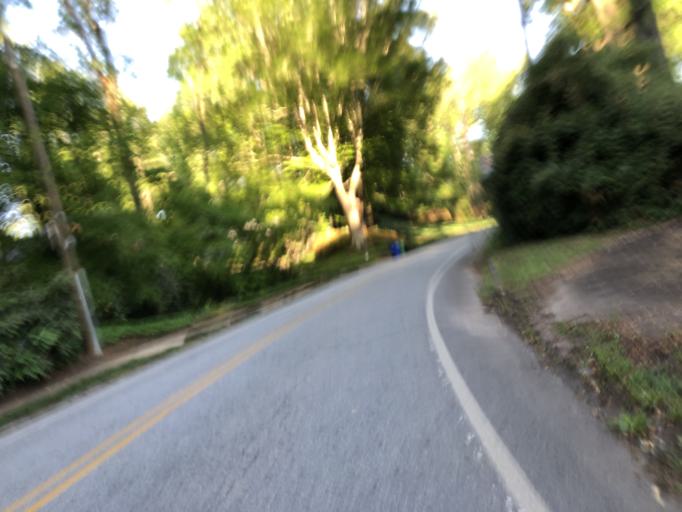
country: US
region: Georgia
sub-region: DeKalb County
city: Druid Hills
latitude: 33.7766
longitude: -84.3255
